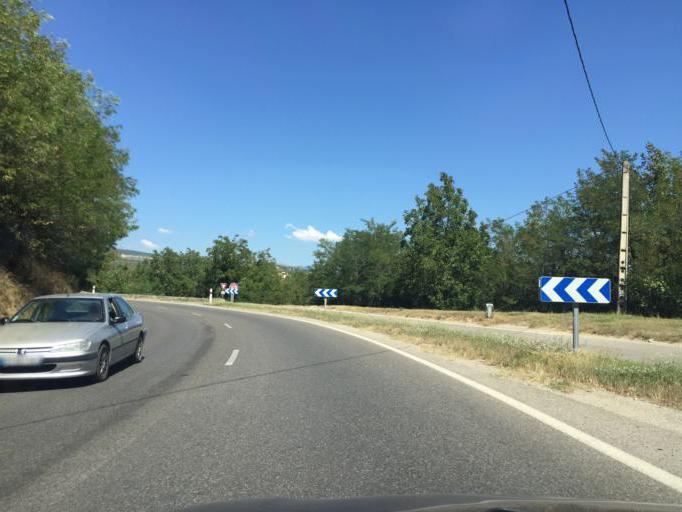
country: FR
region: Provence-Alpes-Cote d'Azur
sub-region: Departement des Alpes-de-Haute-Provence
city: Mane
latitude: 43.9457
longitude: 5.7734
